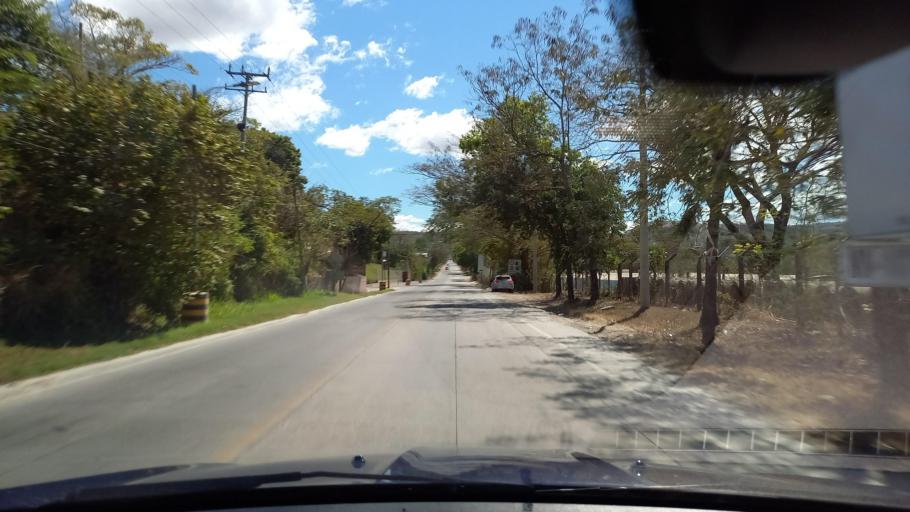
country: SV
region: Santa Ana
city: Metapan
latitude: 14.3414
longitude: -89.4520
